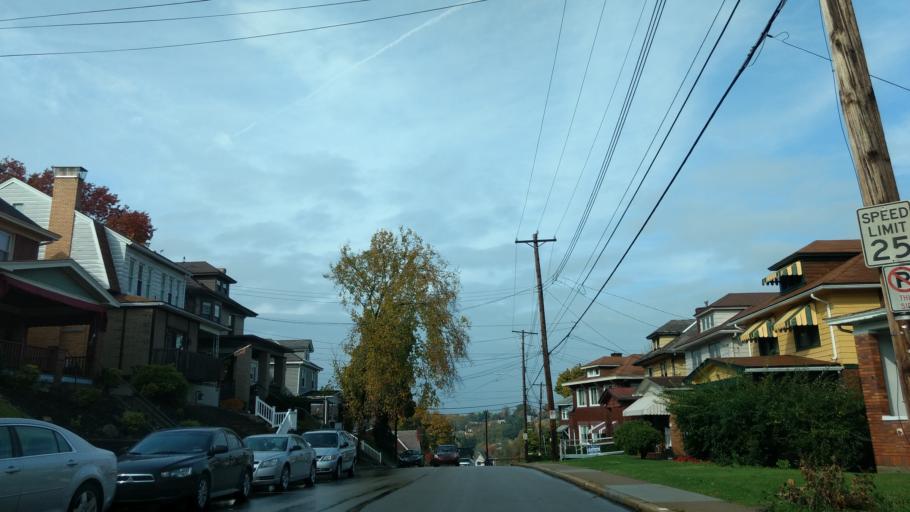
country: US
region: Pennsylvania
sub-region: Allegheny County
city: Dormont
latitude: 40.3996
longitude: -80.0389
